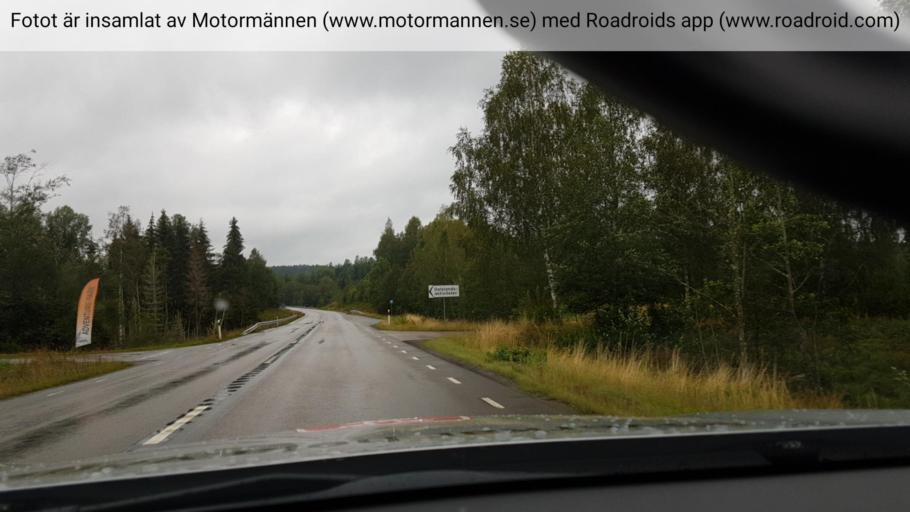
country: SE
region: Vaestra Goetaland
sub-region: Bengtsfors Kommun
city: Billingsfors
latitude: 58.9389
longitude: 12.2059
